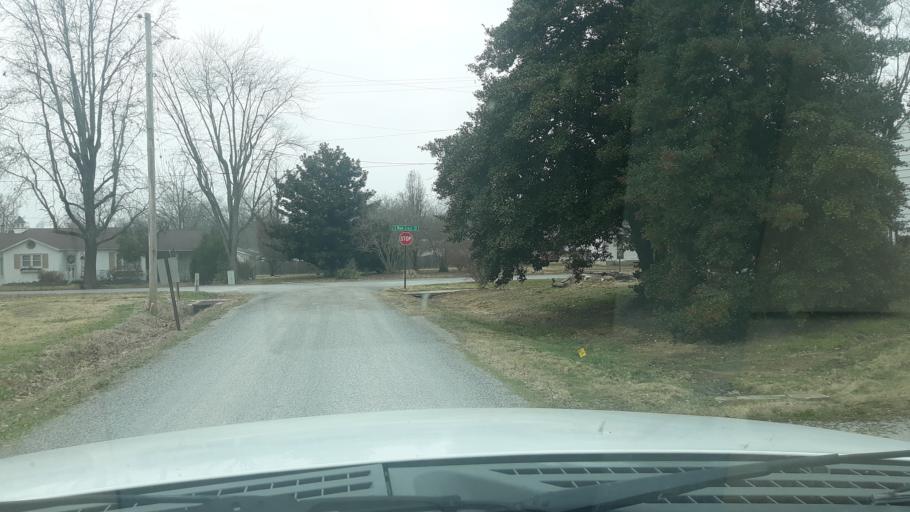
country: US
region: Illinois
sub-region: Saline County
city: Harrisburg
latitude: 37.8376
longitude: -88.6114
